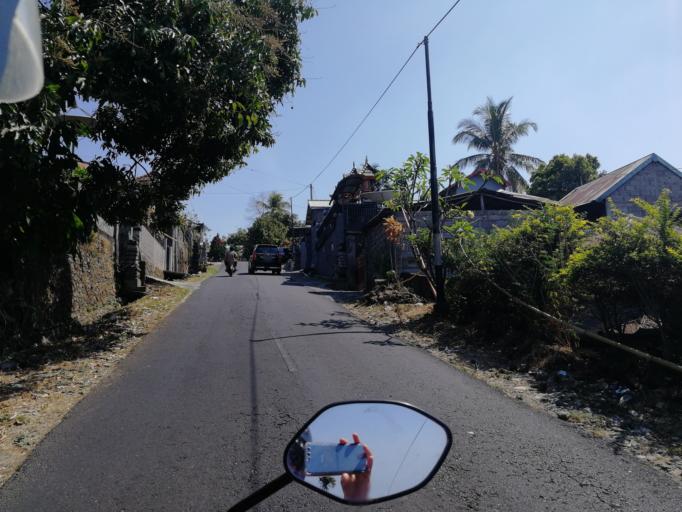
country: ID
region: Bali
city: Banjar Kedisan
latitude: -8.1463
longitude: 115.3069
